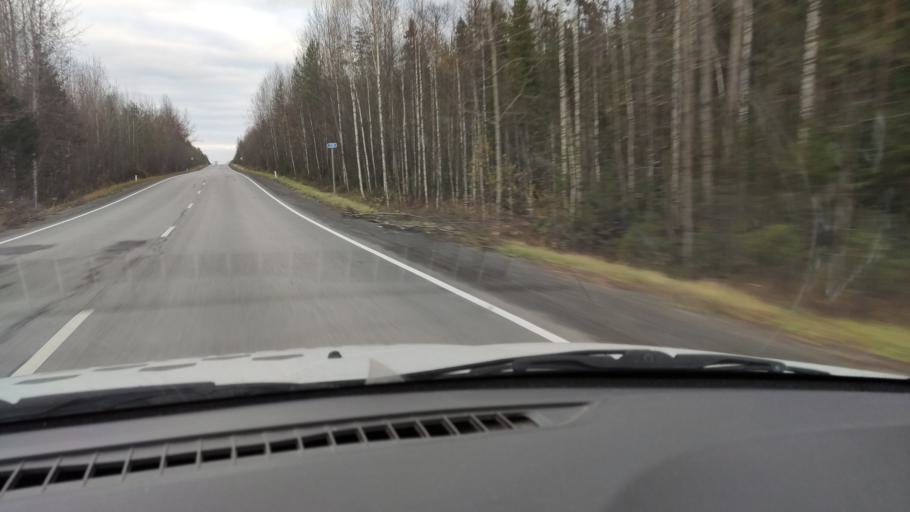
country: RU
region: Kirov
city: Chernaya Kholunitsa
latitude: 58.8645
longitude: 51.5844
